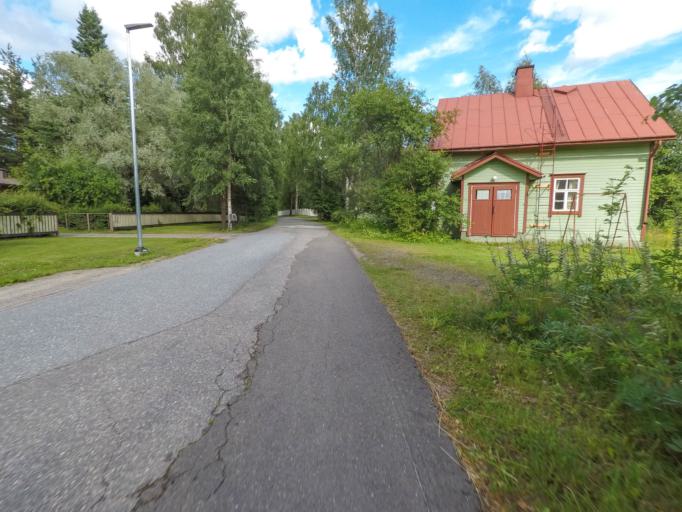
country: FI
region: South Karelia
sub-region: Lappeenranta
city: Joutseno
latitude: 61.1235
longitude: 28.4849
